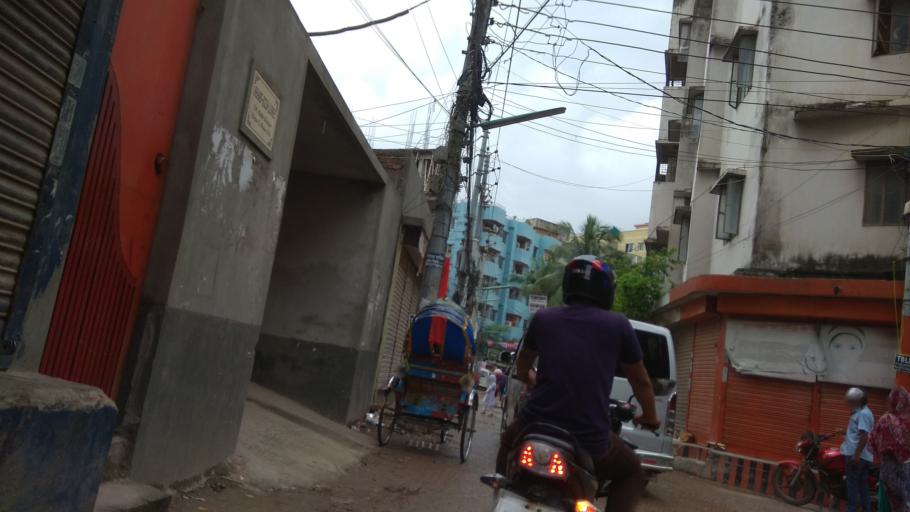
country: BD
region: Dhaka
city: Azimpur
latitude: 23.7972
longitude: 90.3681
